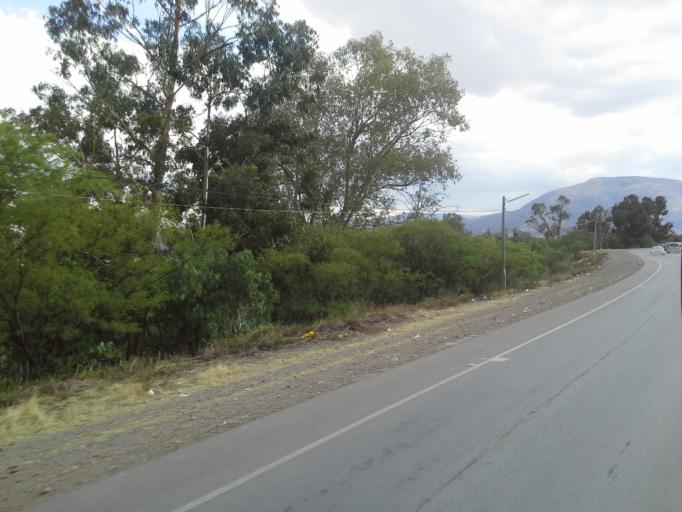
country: BO
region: Cochabamba
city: Tarata
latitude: -17.5420
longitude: -66.0397
